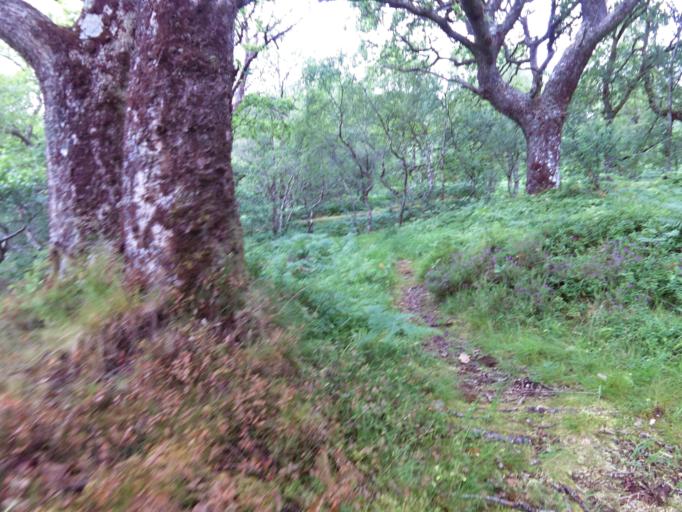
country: GB
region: Scotland
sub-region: Highland
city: Fort William
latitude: 56.8320
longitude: -5.1236
